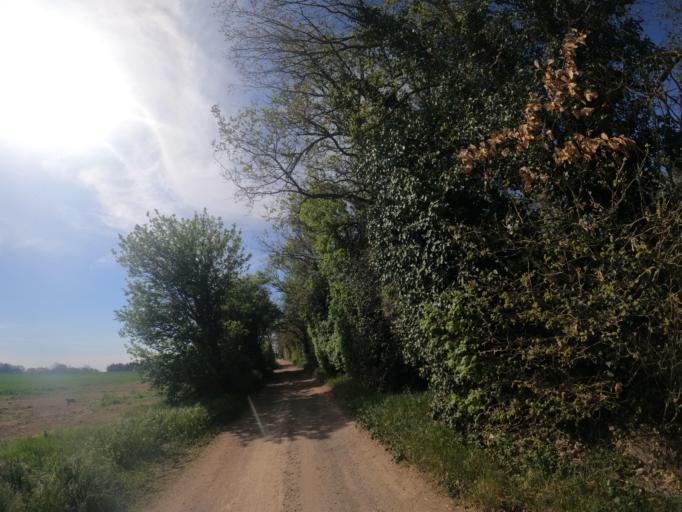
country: FR
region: Poitou-Charentes
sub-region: Departement des Deux-Sevres
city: Saint-Varent
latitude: 46.9141
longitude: -0.2119
